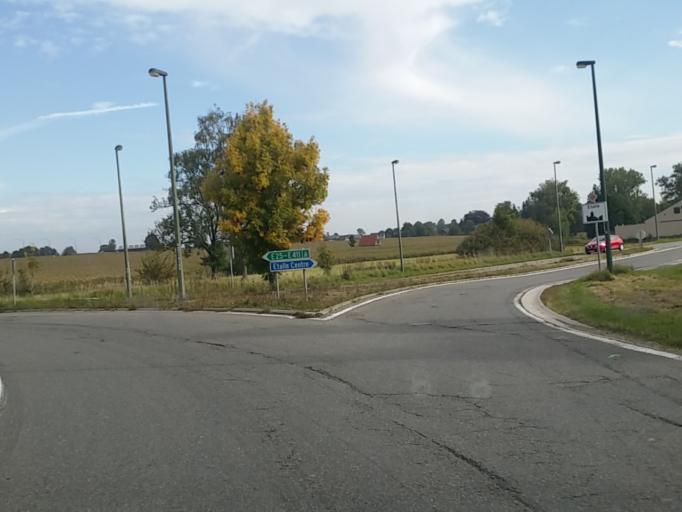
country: BE
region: Wallonia
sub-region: Province du Luxembourg
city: Etalle
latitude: 49.6724
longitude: 5.5907
